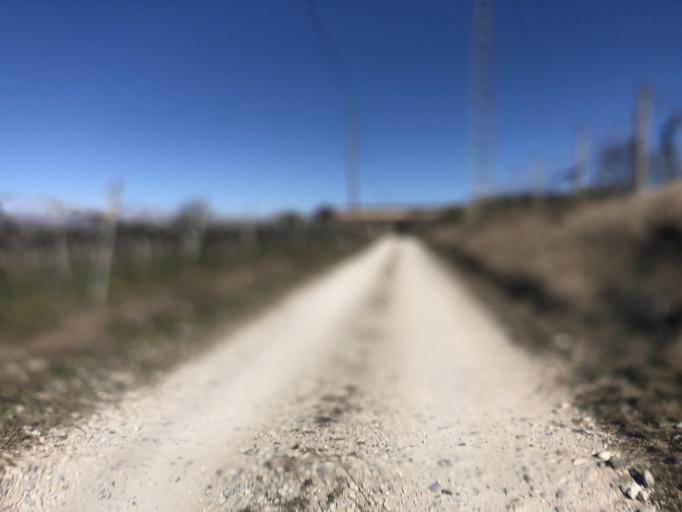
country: IT
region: Veneto
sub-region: Provincia di Verona
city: San Giorgio in Salici
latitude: 45.4262
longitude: 10.8085
